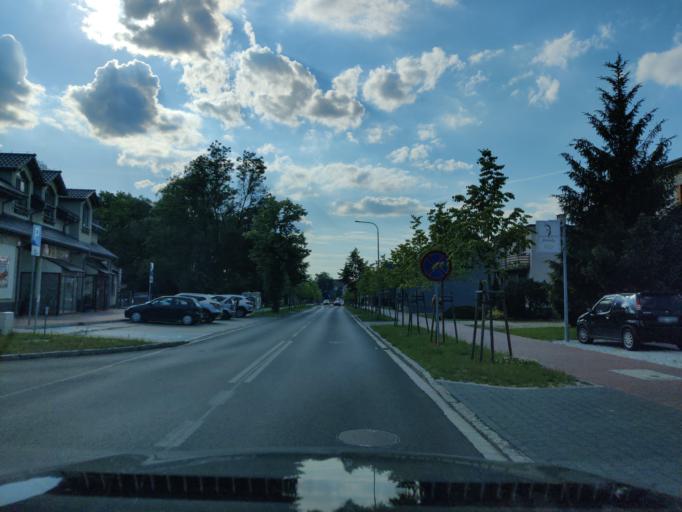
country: PL
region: Greater Poland Voivodeship
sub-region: Powiat wolsztynski
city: Wolsztyn
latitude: 52.1133
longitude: 16.1210
